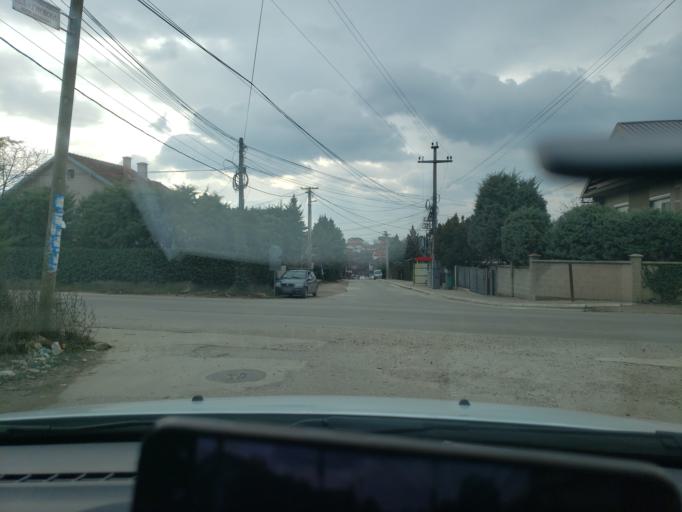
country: MK
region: Kumanovo
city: Kumanovo
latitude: 42.1449
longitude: 21.7415
